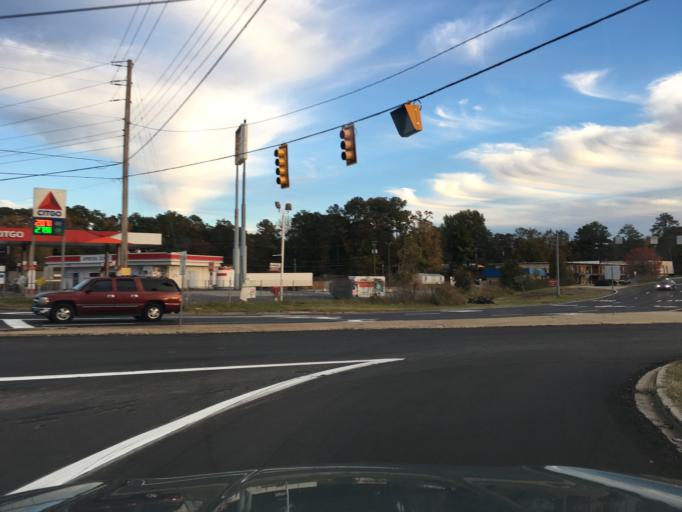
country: US
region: South Carolina
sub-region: Lexington County
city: Saint Andrews
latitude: 34.0302
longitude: -81.1015
